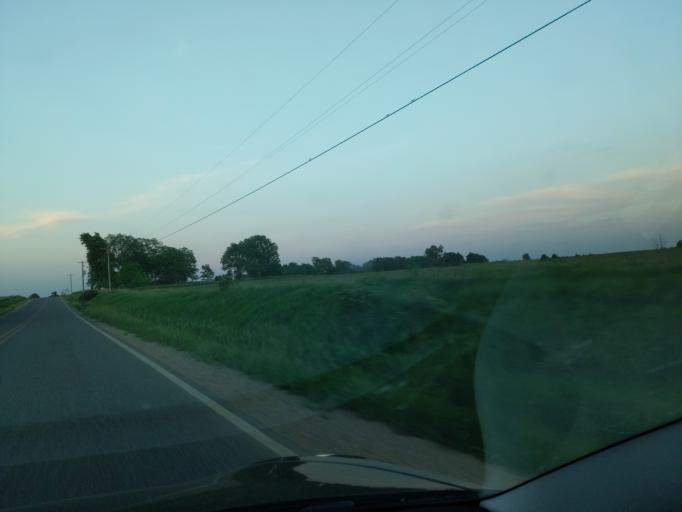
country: US
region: Michigan
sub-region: Barry County
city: Nashville
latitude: 42.5381
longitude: -85.0803
